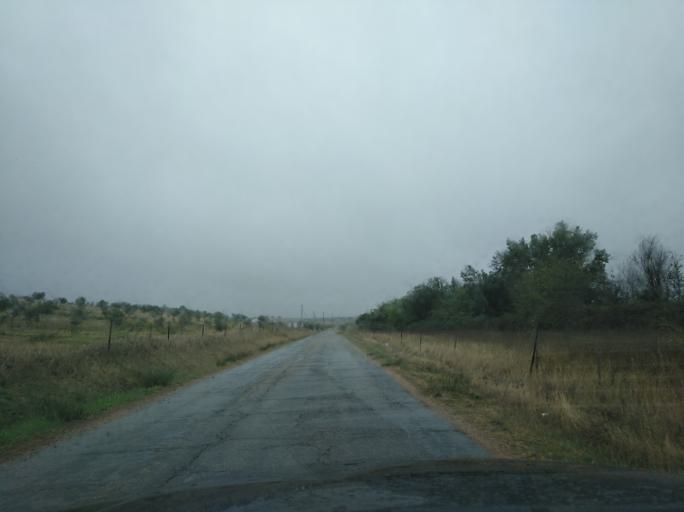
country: PT
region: Portalegre
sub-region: Campo Maior
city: Campo Maior
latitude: 38.9794
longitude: -7.0694
